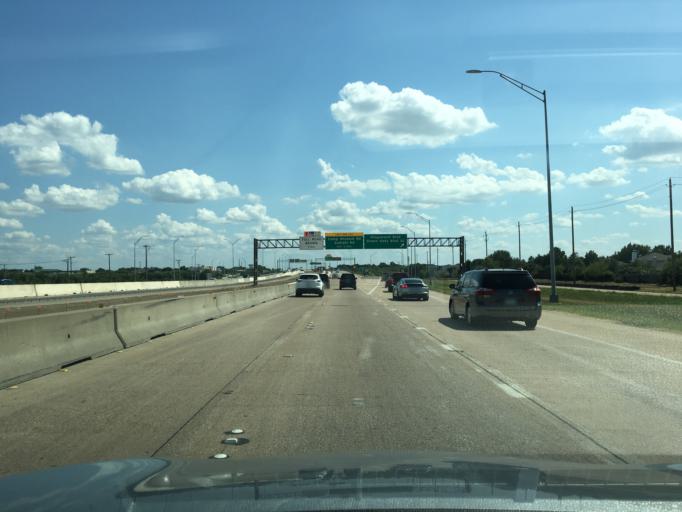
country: US
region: Texas
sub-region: Tarrant County
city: Arlington
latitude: 32.6676
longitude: -97.0629
